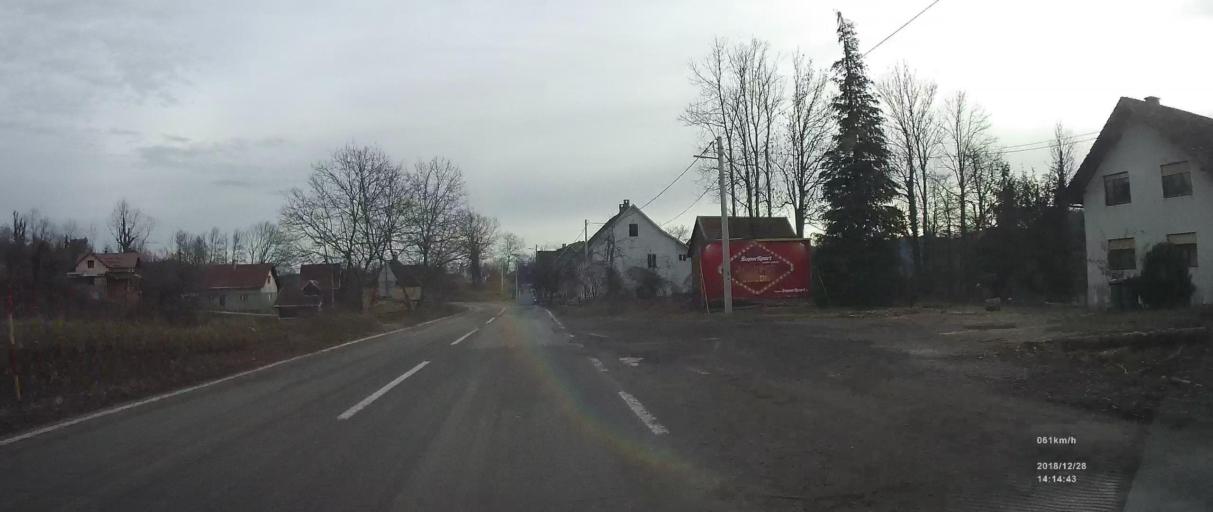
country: HR
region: Primorsko-Goranska
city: Vrbovsko
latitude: 45.4299
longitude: 15.0217
